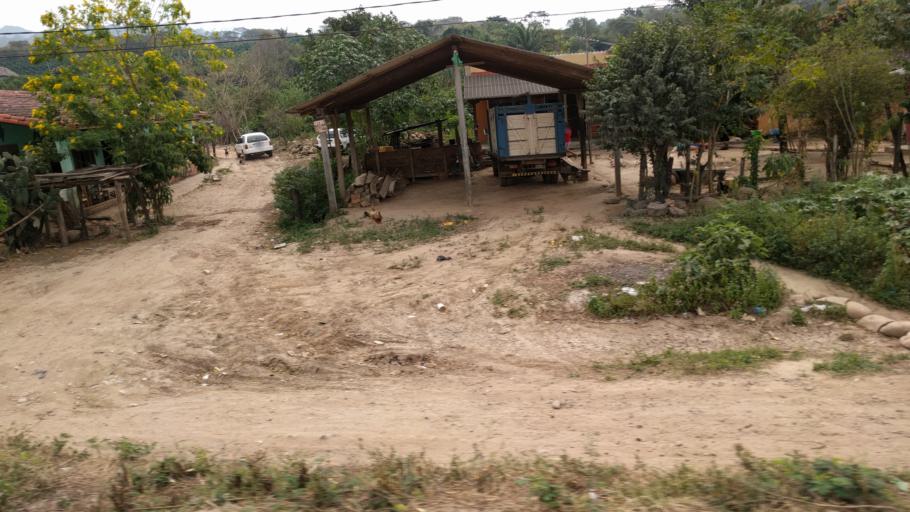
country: BO
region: Santa Cruz
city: Jorochito
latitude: -18.1500
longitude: -63.4890
